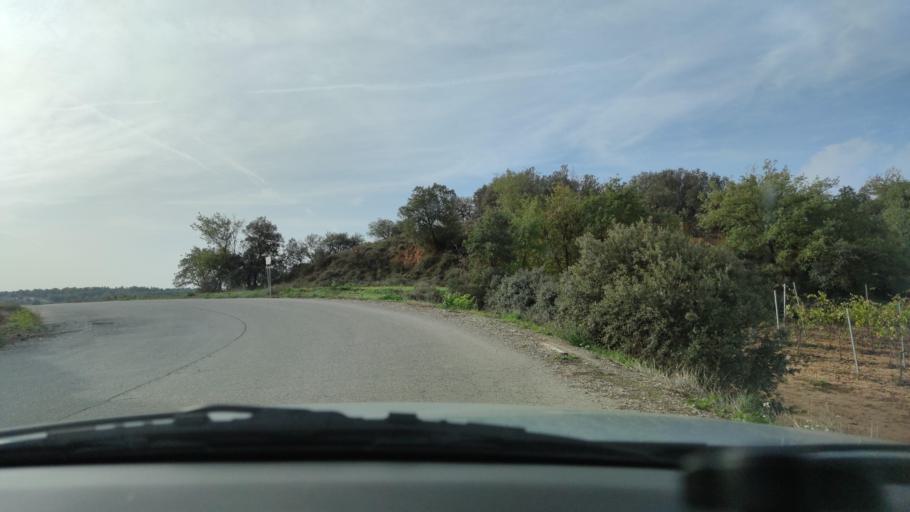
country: ES
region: Catalonia
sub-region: Provincia de Lleida
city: Artesa de Segre
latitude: 41.9144
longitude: 1.0294
